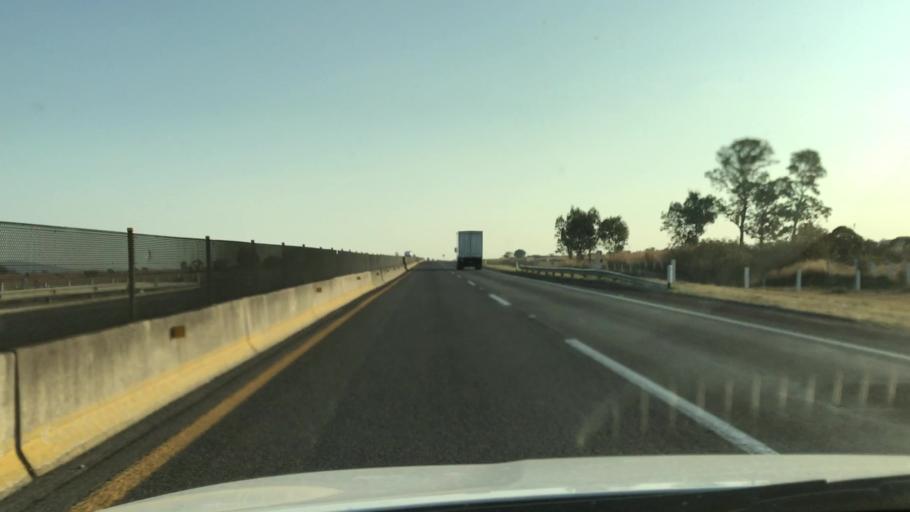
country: MX
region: Jalisco
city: Acatic
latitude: 20.7270
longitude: -102.9280
